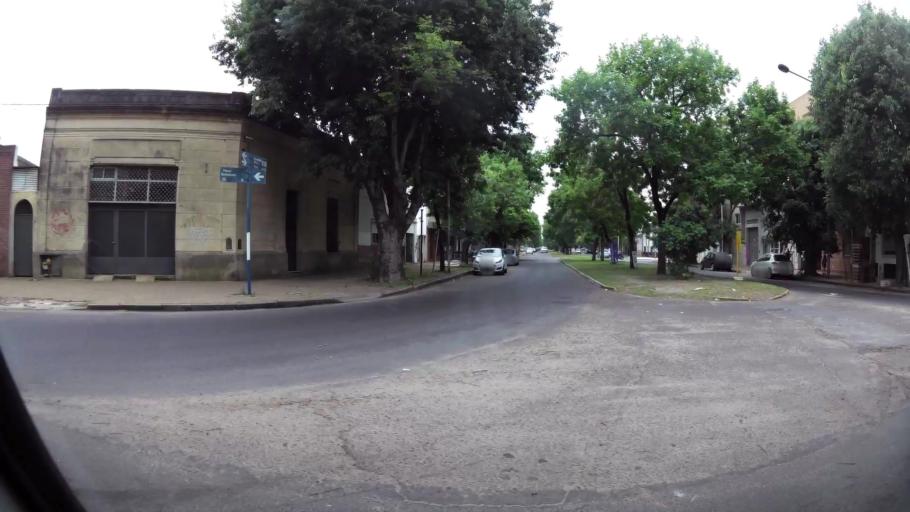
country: AR
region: Buenos Aires
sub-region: Partido de La Plata
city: La Plata
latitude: -34.9373
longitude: -57.9595
